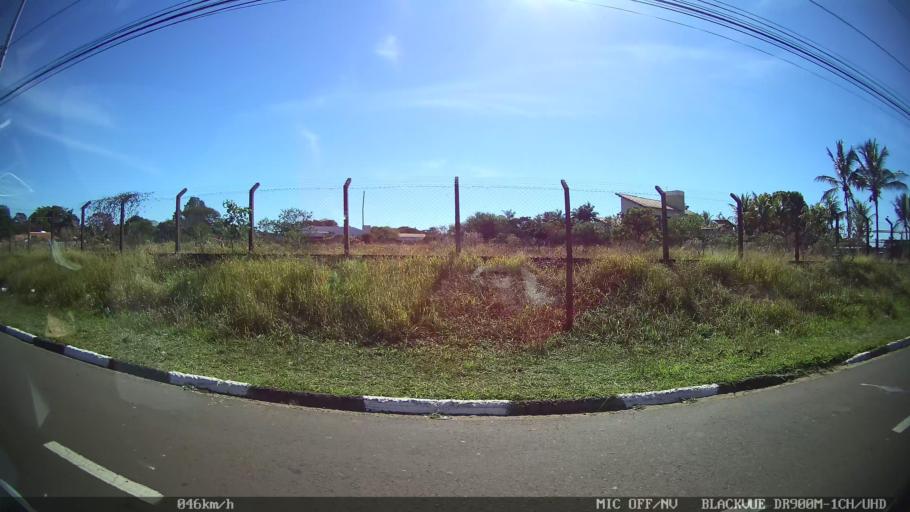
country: BR
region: Sao Paulo
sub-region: Franca
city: Franca
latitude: -20.5644
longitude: -47.3600
